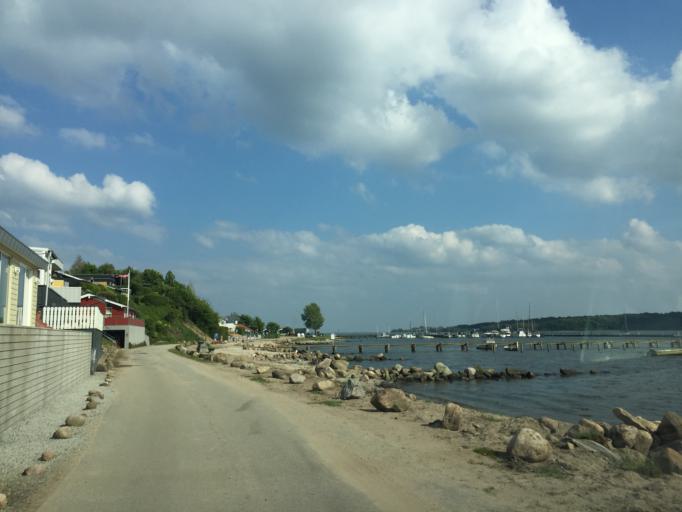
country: DK
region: South Denmark
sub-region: Aabenraa Kommune
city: Lojt Kirkeby
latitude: 55.1315
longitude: 9.4776
